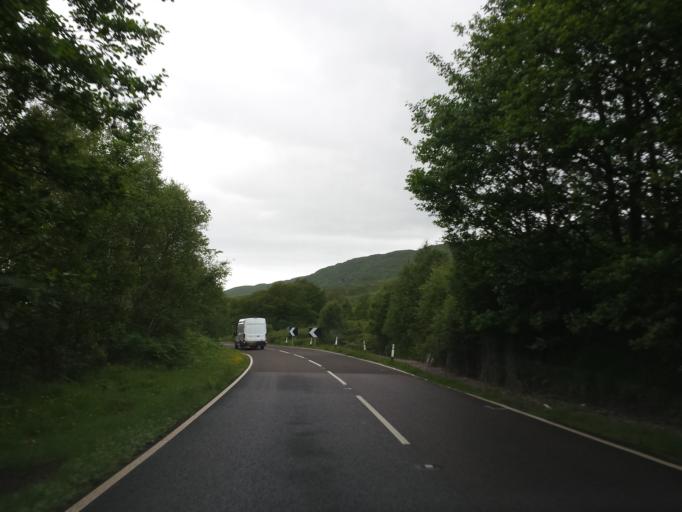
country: GB
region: Scotland
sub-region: Argyll and Bute
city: Isle Of Mull
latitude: 56.8835
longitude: -5.6097
